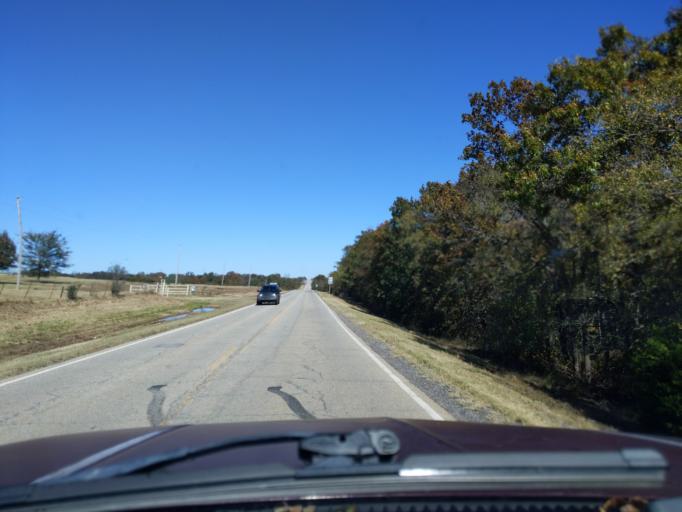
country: US
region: Oklahoma
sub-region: Creek County
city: Bristow
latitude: 35.7266
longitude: -96.3872
